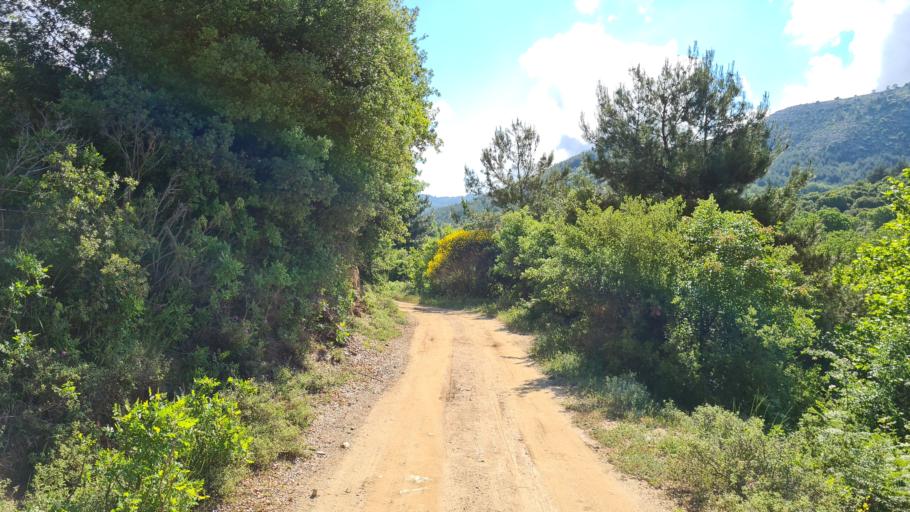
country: GR
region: East Macedonia and Thrace
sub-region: Nomos Kavalas
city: Potamia
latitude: 40.6631
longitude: 24.7044
